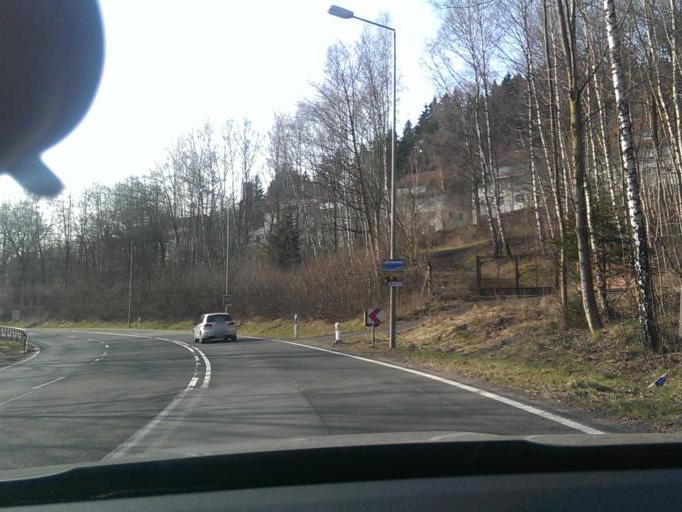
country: DE
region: Thuringia
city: Suhl
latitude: 50.5996
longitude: 10.7197
